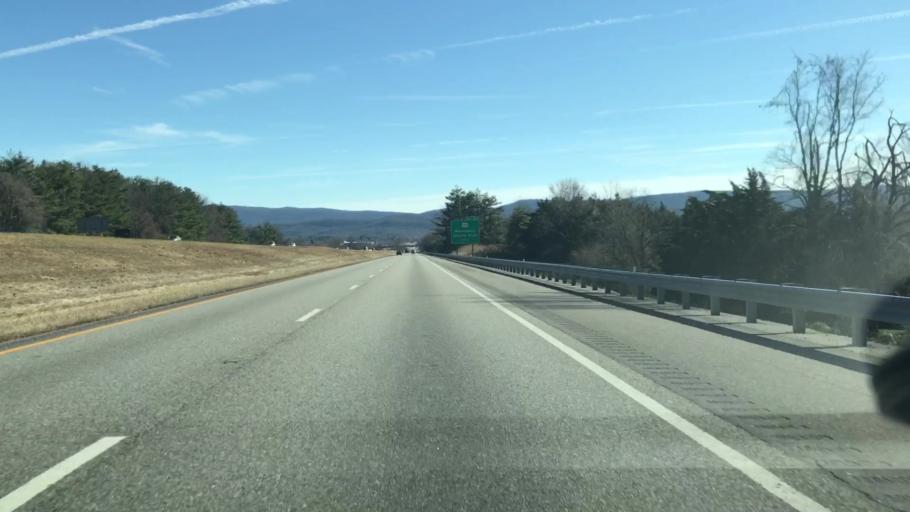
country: US
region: Virginia
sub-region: Augusta County
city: Fishersville
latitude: 38.0662
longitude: -78.9587
